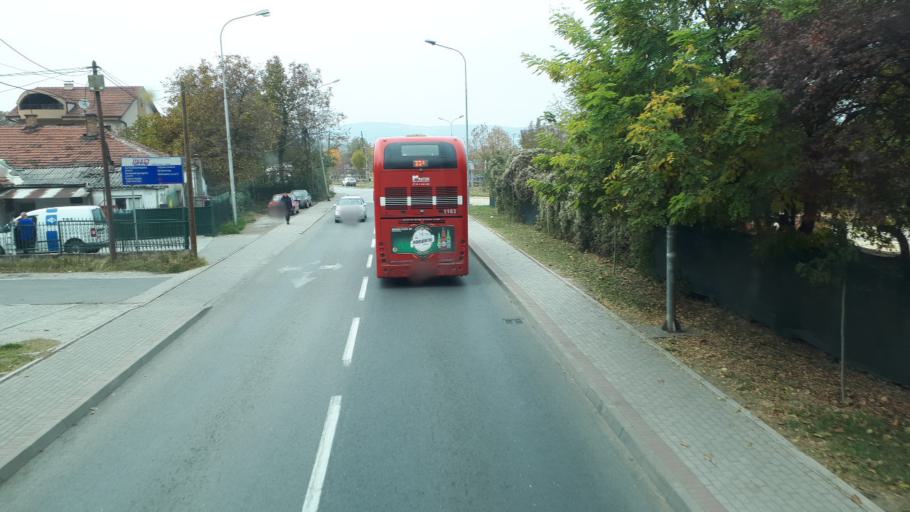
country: MK
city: Krushopek
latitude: 42.0104
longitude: 21.3611
